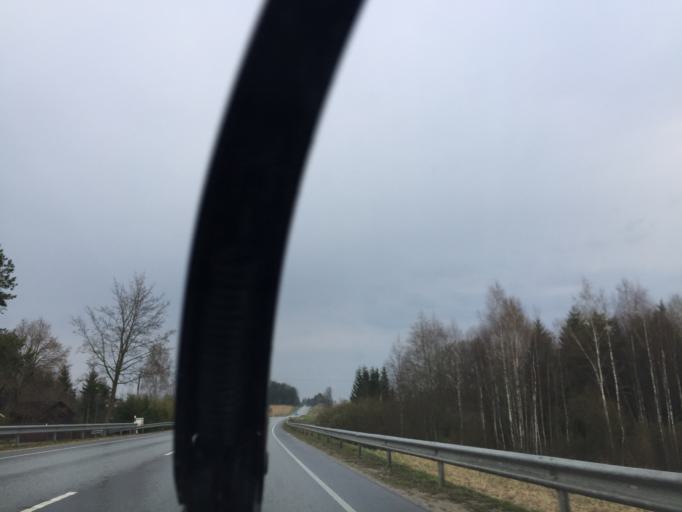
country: EE
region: Tartu
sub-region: UElenurme vald
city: Ulenurme
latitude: 58.1917
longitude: 26.6963
